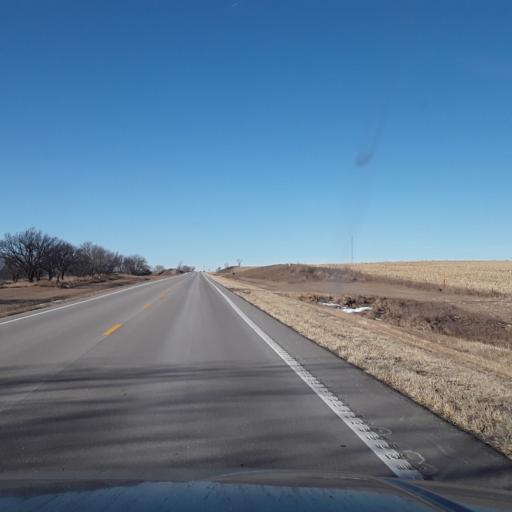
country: US
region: Nebraska
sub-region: Dawson County
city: Cozad
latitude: 40.6929
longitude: -100.1482
